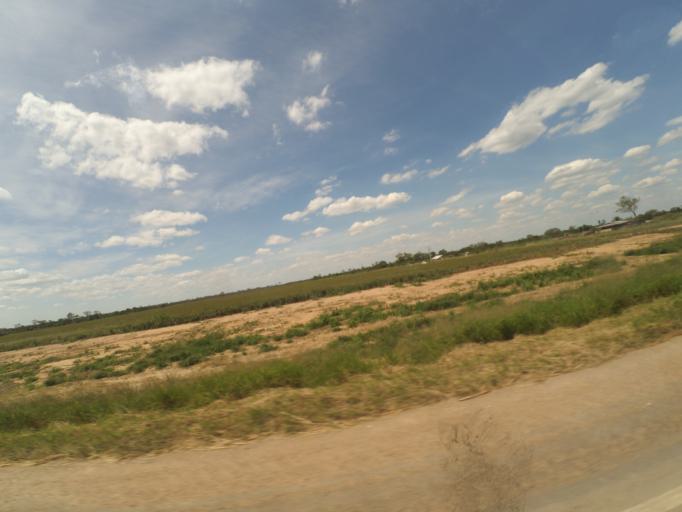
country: BO
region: Santa Cruz
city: Pailon
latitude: -17.5890
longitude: -61.9546
